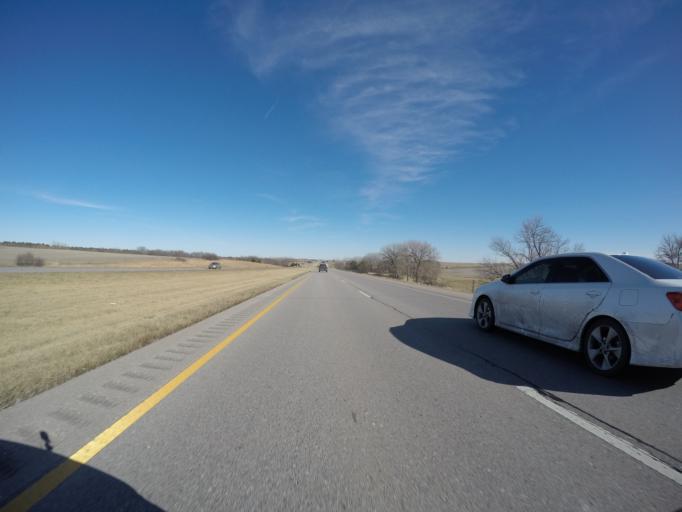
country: US
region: Nebraska
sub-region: Seward County
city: Milford
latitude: 40.8213
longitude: -96.9727
